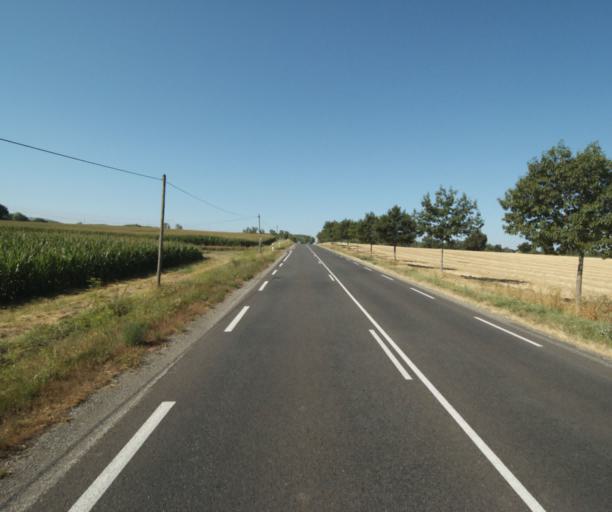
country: FR
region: Midi-Pyrenees
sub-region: Departement du Tarn
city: Soreze
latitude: 43.4929
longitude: 2.0404
